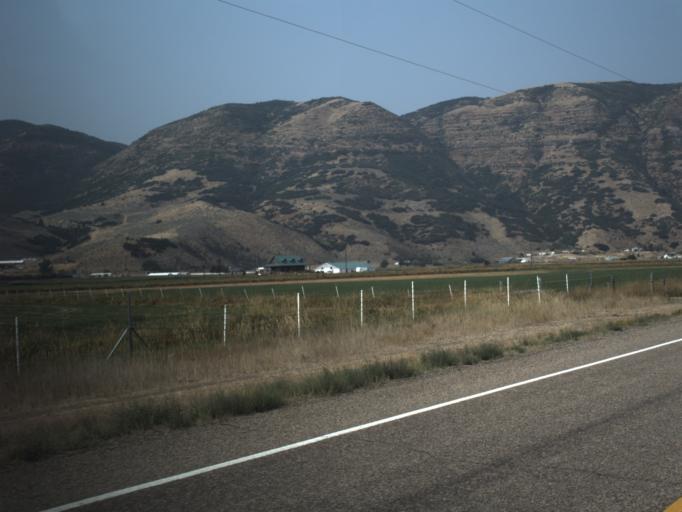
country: US
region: Utah
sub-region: Summit County
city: Coalville
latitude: 41.0319
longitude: -111.5121
